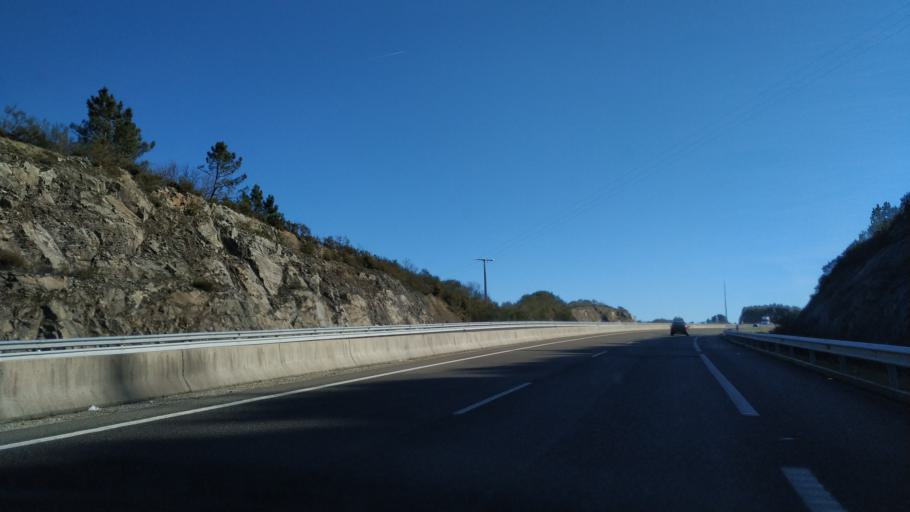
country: ES
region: Galicia
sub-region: Provincia de Pontevedra
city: Dozon
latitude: 42.5654
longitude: -8.0480
